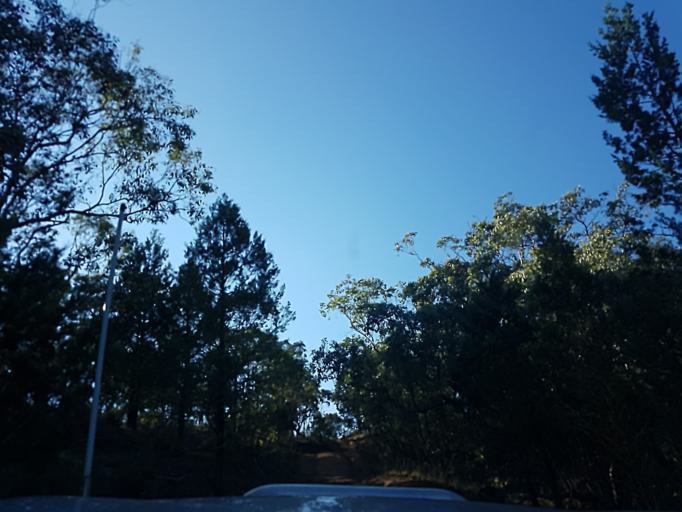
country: AU
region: New South Wales
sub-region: Snowy River
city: Jindabyne
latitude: -36.9575
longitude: 148.3762
